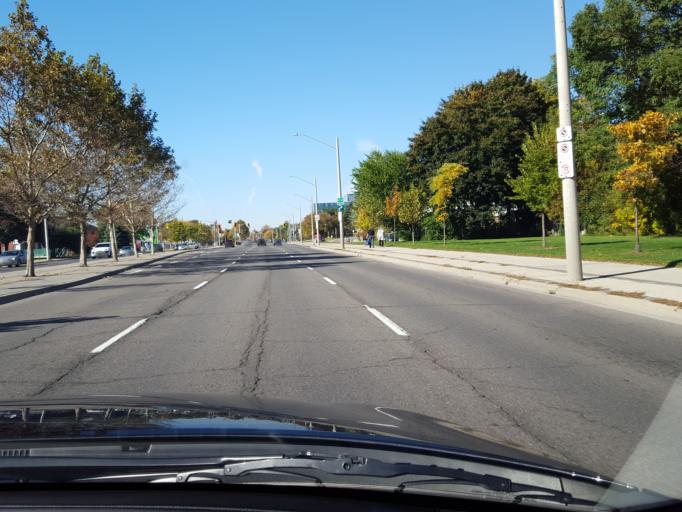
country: CA
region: Ontario
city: Hamilton
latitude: 43.2579
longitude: -79.9144
